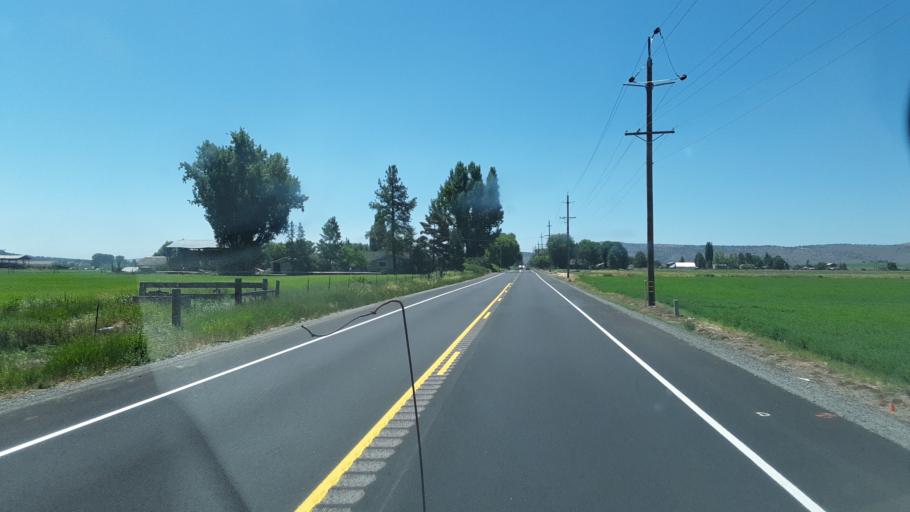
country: US
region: Oregon
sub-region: Klamath County
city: Altamont
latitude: 42.1353
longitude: -121.6984
